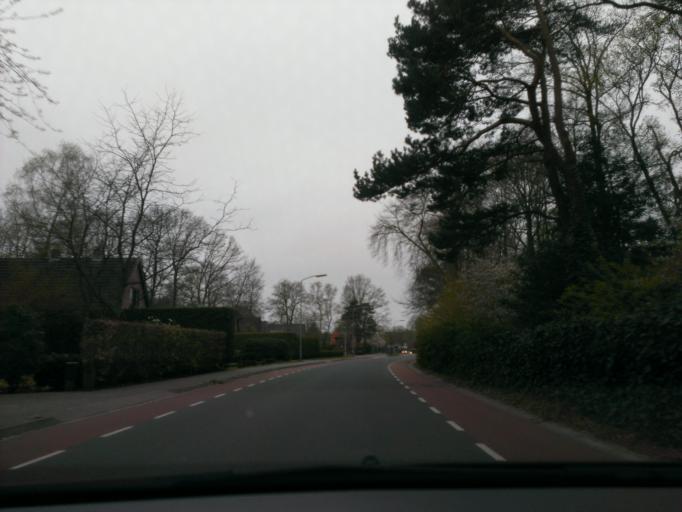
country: NL
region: Gelderland
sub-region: Gemeente Epe
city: Vaassen
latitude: 52.2814
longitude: 5.9676
